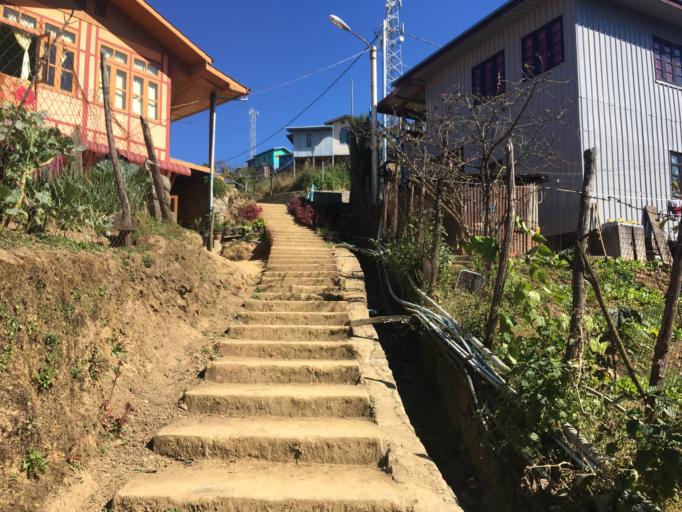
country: MM
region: Chin
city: Hakha
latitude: 22.6380
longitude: 93.6051
